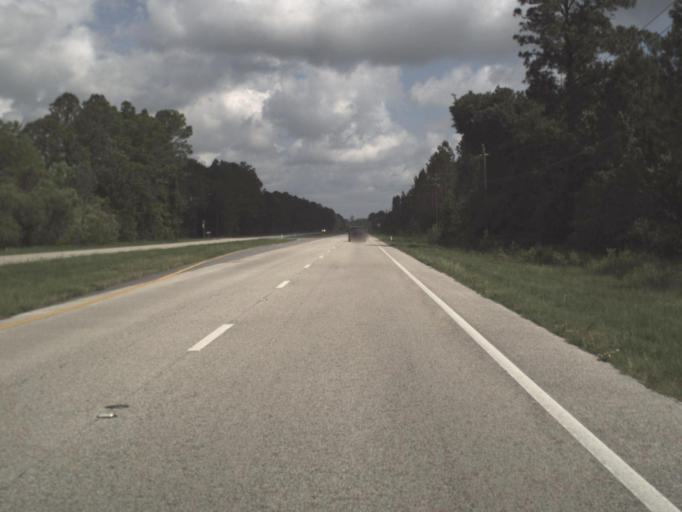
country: US
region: Florida
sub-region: Saint Johns County
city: Butler Beach
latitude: 29.7118
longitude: -81.3015
